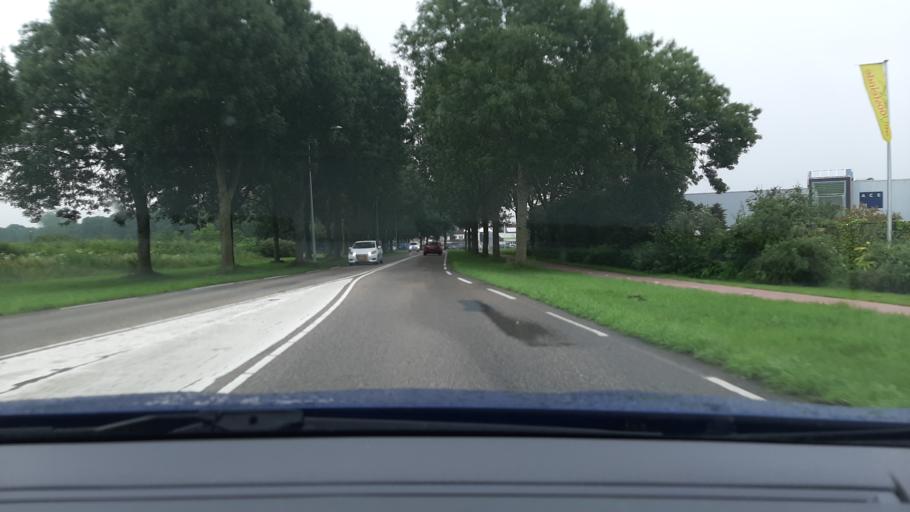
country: NL
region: Flevoland
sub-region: Gemeente Zeewolde
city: Zeewolde
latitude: 52.3380
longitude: 5.5284
